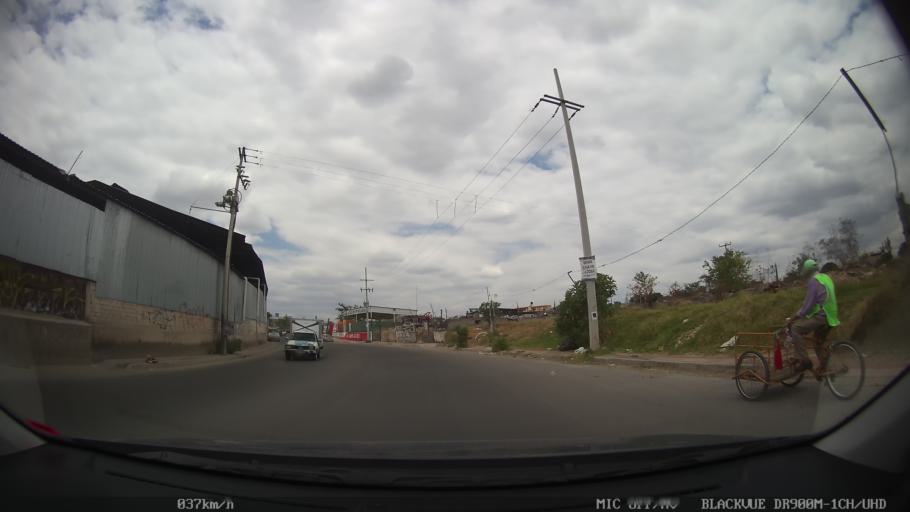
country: MX
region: Jalisco
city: Tlaquepaque
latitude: 20.6524
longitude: -103.2704
